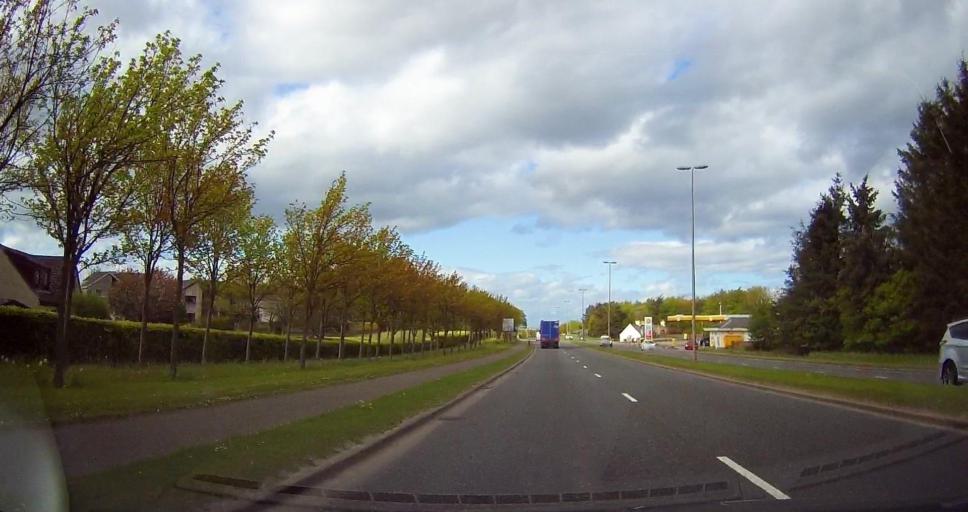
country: GB
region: Scotland
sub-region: Aberdeen City
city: Aberdeen
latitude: 57.1133
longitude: -2.0898
